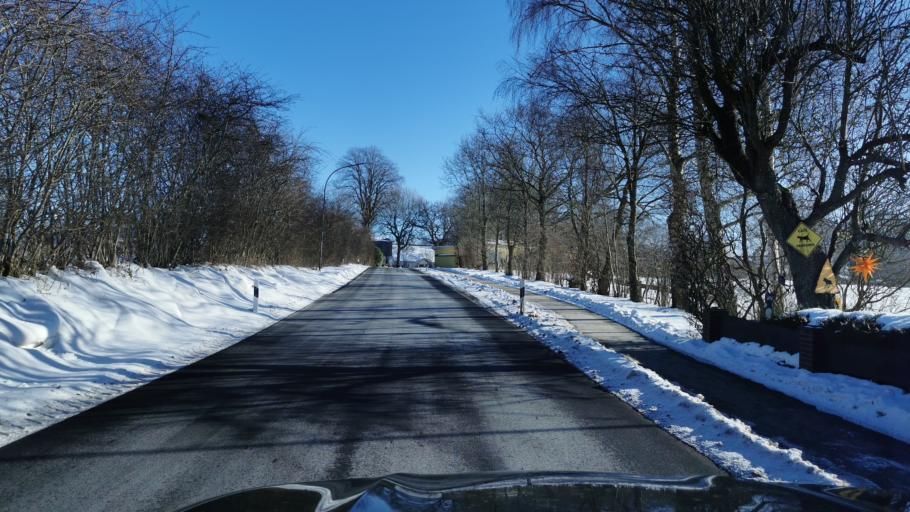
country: DE
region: Schleswig-Holstein
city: Sorup
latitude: 54.7308
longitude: 9.6520
